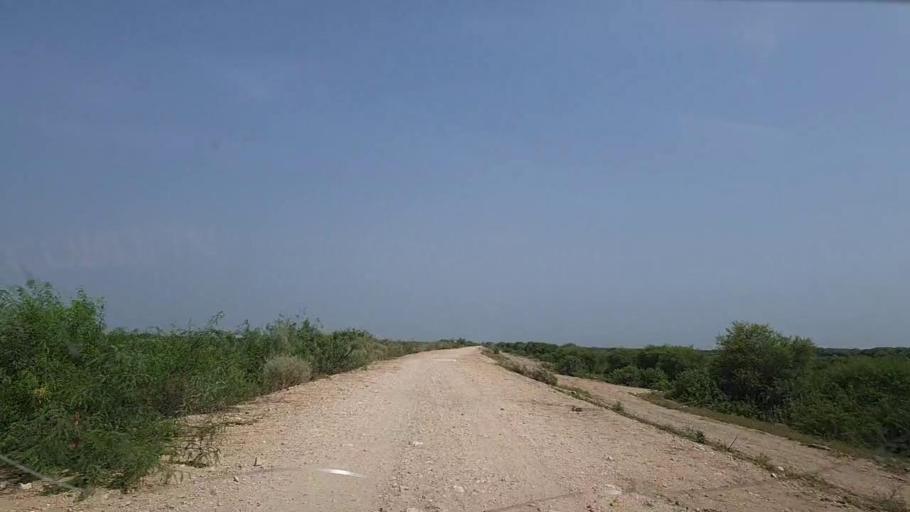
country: PK
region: Sindh
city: Ghotki
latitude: 28.1118
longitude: 69.3918
